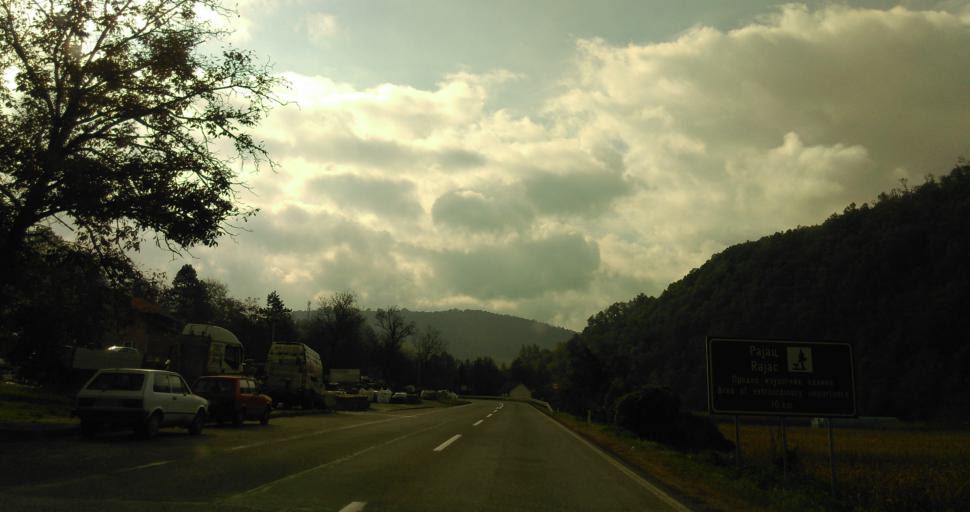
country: RS
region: Central Serbia
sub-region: Kolubarski Okrug
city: Ljig
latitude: 44.2053
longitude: 20.2257
